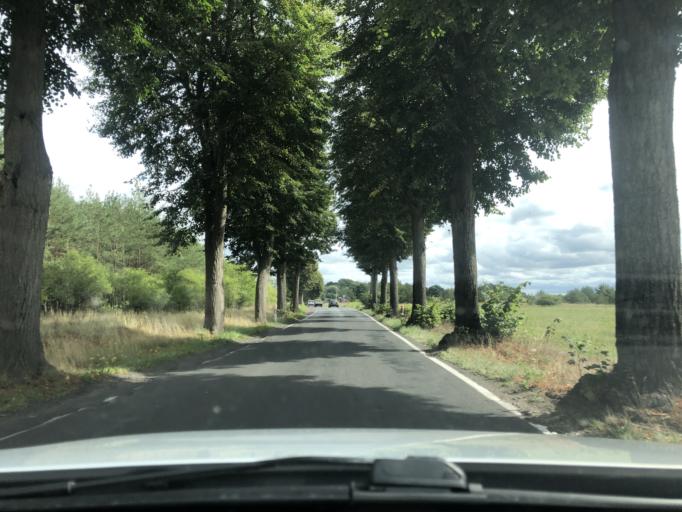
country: PL
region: Greater Poland Voivodeship
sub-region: Powiat czarnkowsko-trzcianecki
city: Wielen
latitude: 52.9037
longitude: 16.1519
